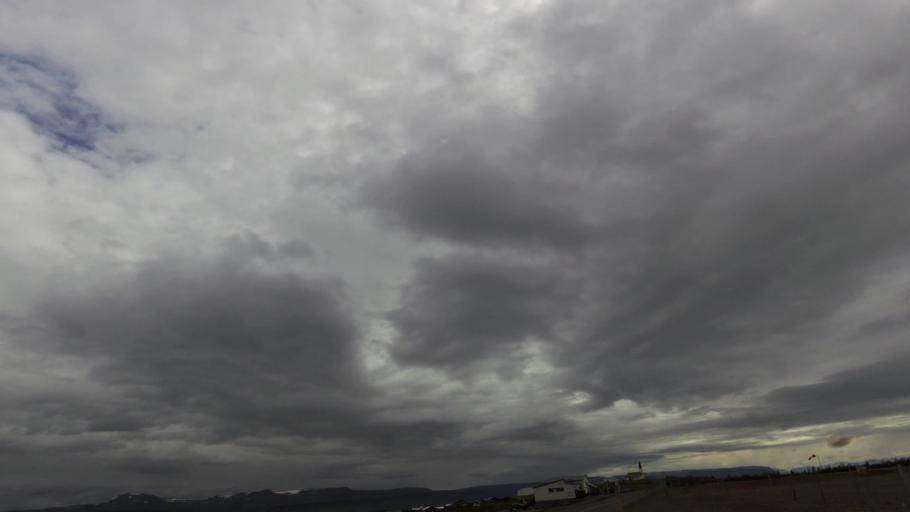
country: IS
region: West
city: Stykkisholmur
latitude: 65.4538
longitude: -22.2006
